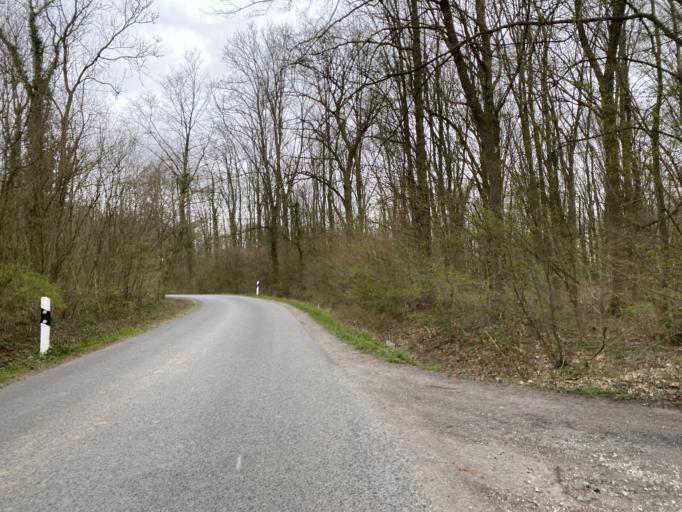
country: DE
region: North Rhine-Westphalia
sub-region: Regierungsbezirk Arnsberg
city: Welver
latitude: 51.6825
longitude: 7.9142
